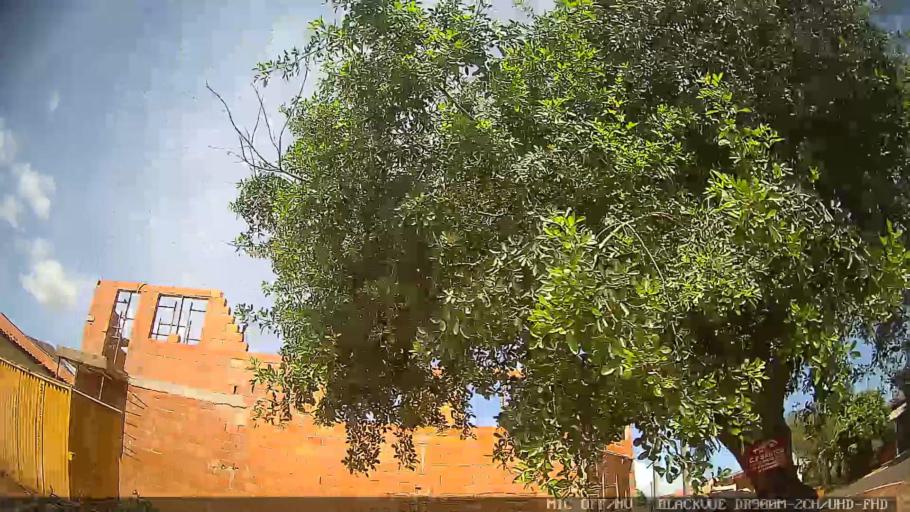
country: BR
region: Sao Paulo
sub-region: Artur Nogueira
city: Artur Nogueira
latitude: -22.6113
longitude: -47.0660
